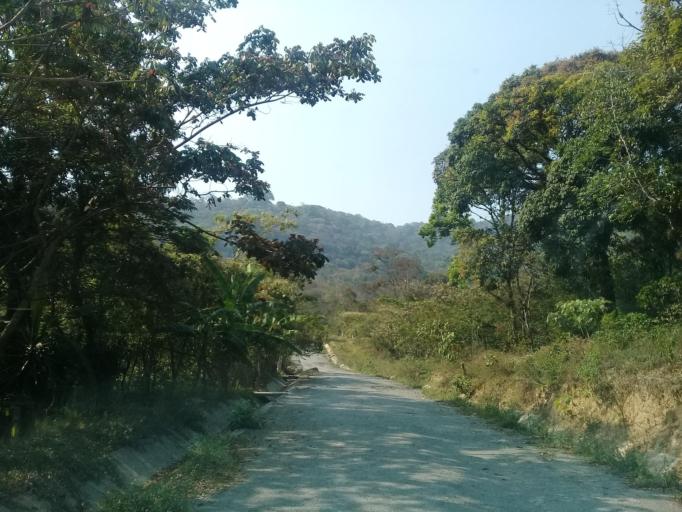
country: MX
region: Veracruz
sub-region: Ixtaczoquitlan
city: Campo Chico
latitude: 18.8397
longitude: -97.0297
